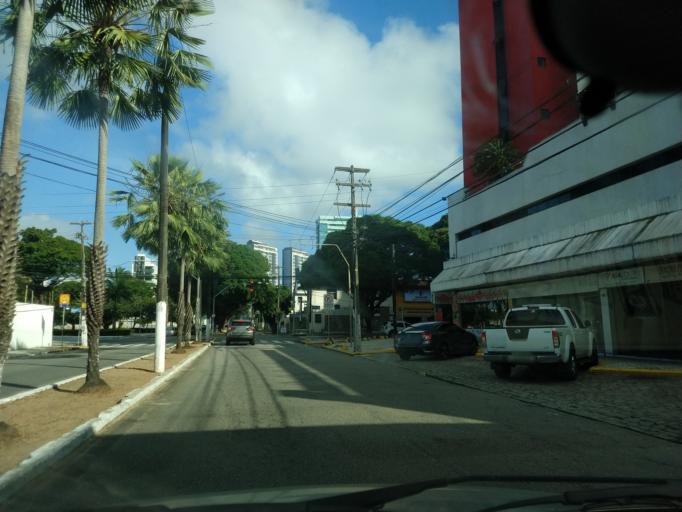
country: BR
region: Rio Grande do Norte
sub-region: Natal
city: Natal
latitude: -5.7844
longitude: -35.1994
